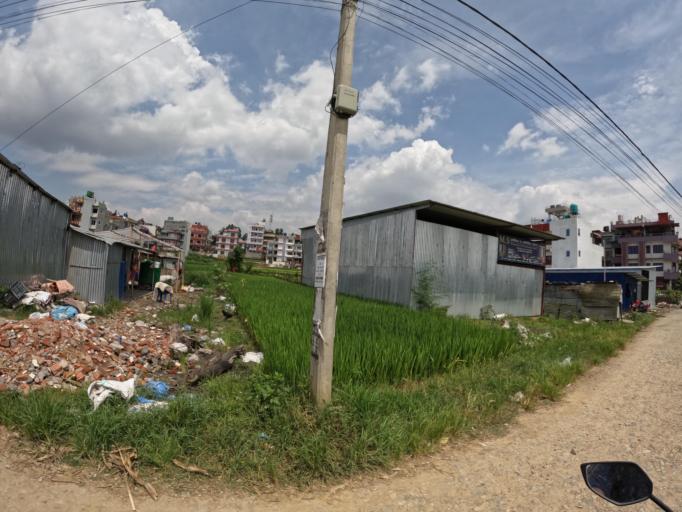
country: NP
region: Central Region
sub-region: Bagmati Zone
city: Bhaktapur
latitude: 27.6793
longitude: 85.3735
